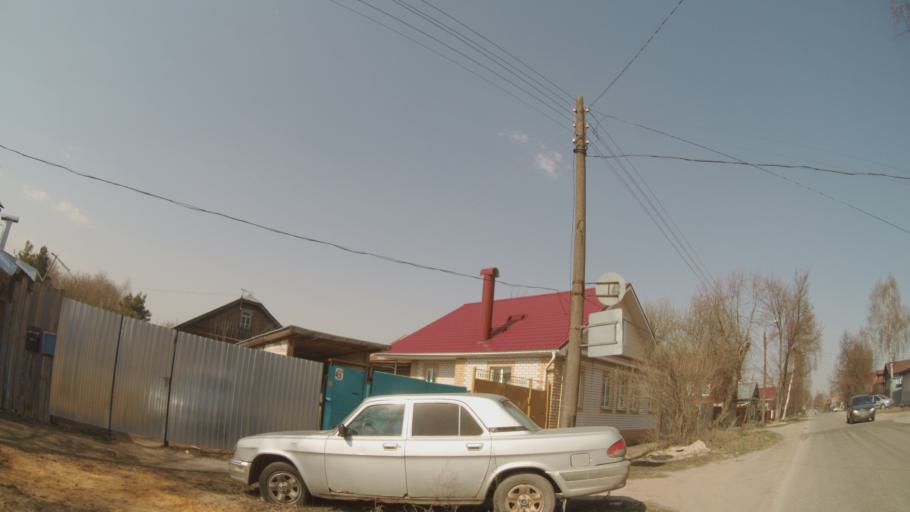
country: RU
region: Nizjnij Novgorod
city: Arzamas
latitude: 55.3874
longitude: 43.8239
